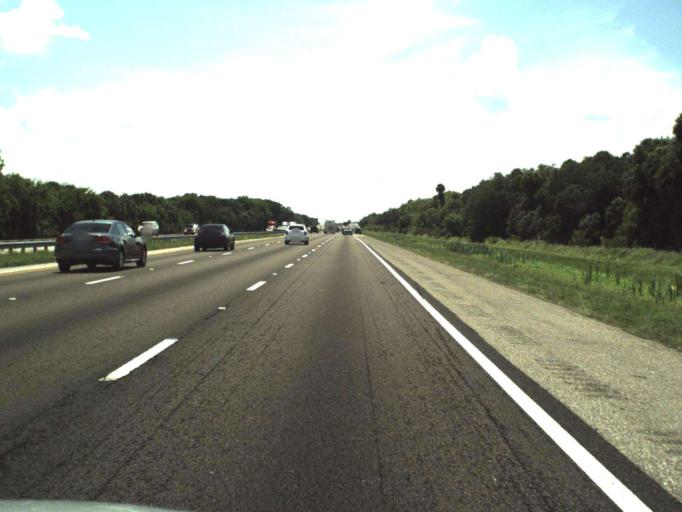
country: US
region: Florida
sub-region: Volusia County
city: DeBary
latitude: 28.8511
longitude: -81.3038
